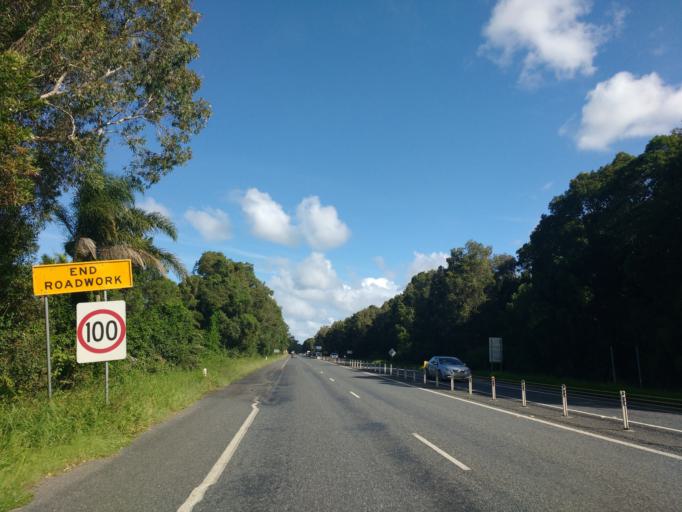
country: AU
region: New South Wales
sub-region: Ballina
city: Ballina
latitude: -28.9047
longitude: 153.4796
